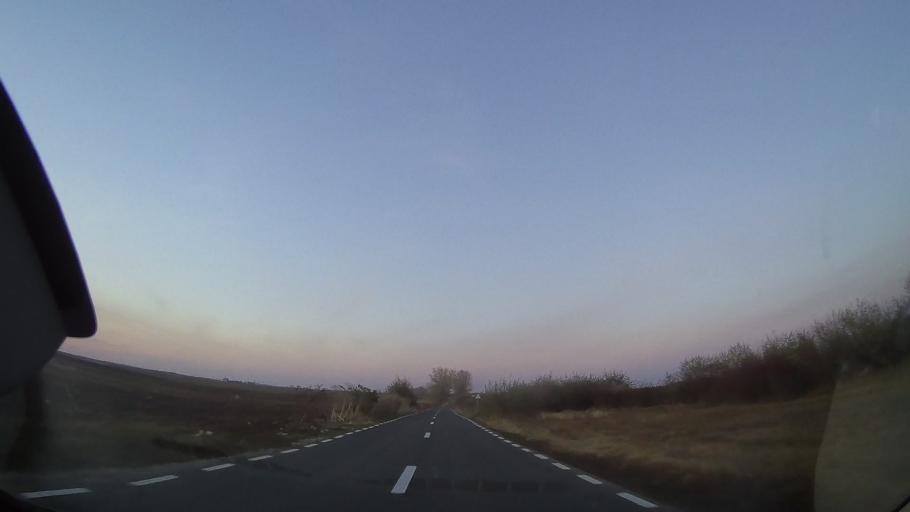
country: RO
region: Constanta
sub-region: Comuna Cobadin
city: Cobadin
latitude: 44.0364
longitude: 28.2592
